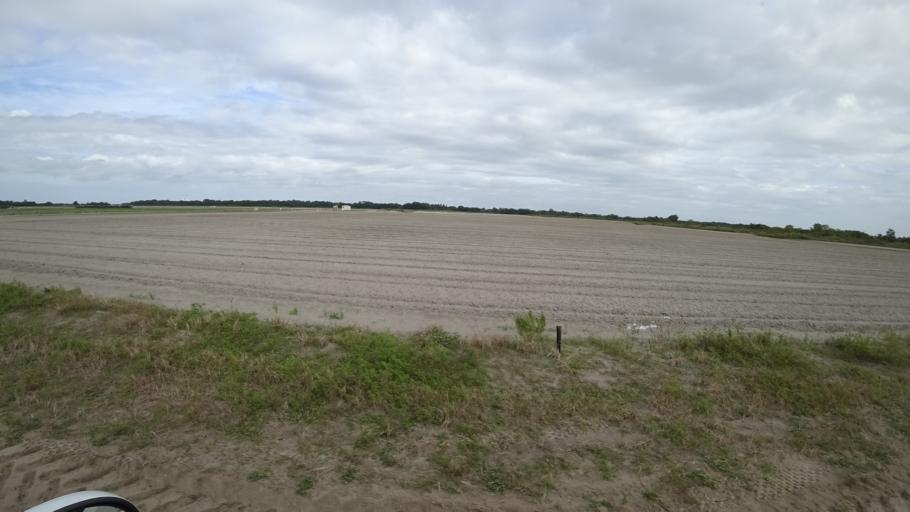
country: US
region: Florida
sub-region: Hillsborough County
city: Wimauma
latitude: 27.5625
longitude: -82.3012
